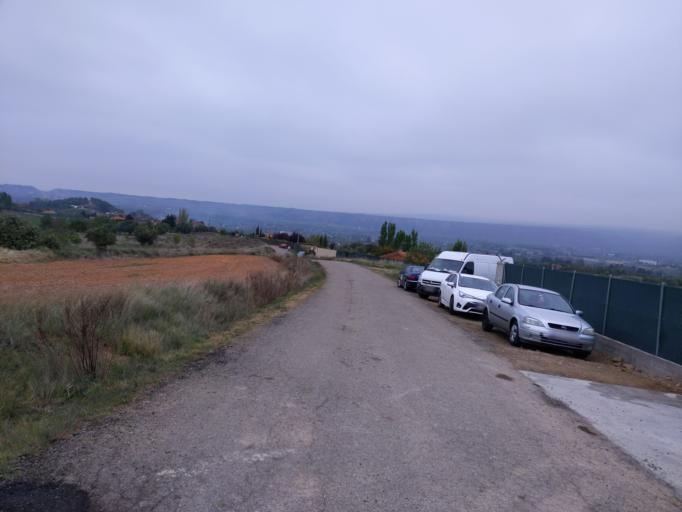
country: ES
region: La Rioja
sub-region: Provincia de La Rioja
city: Lardero
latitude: 42.4080
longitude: -2.4870
